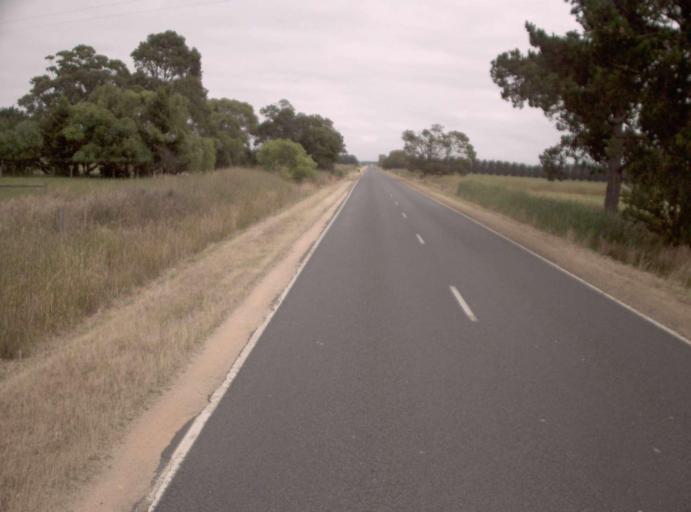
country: AU
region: Victoria
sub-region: Wellington
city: Sale
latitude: -38.0693
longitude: 146.9793
